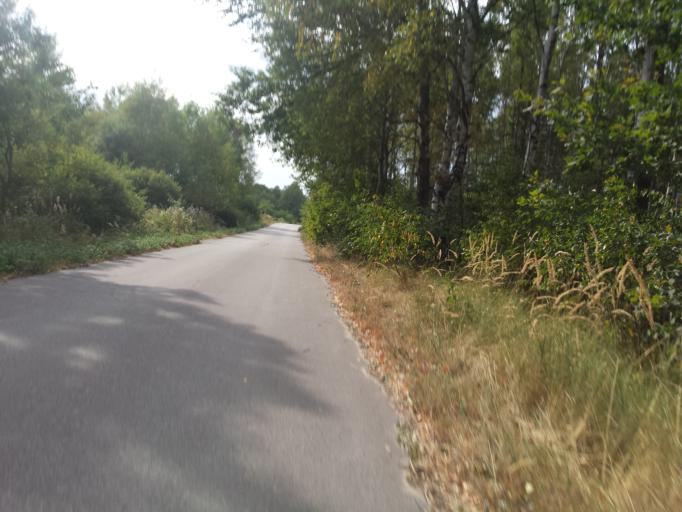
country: PL
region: Swietokrzyskie
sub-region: Powiat kielecki
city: Rakow
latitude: 50.6673
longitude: 21.1382
